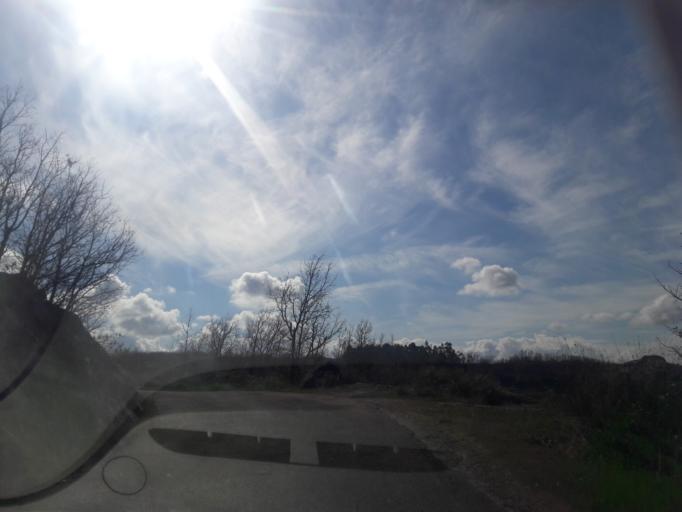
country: ES
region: Castille and Leon
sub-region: Provincia de Salamanca
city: San Esteban de la Sierra
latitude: 40.5068
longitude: -5.8738
